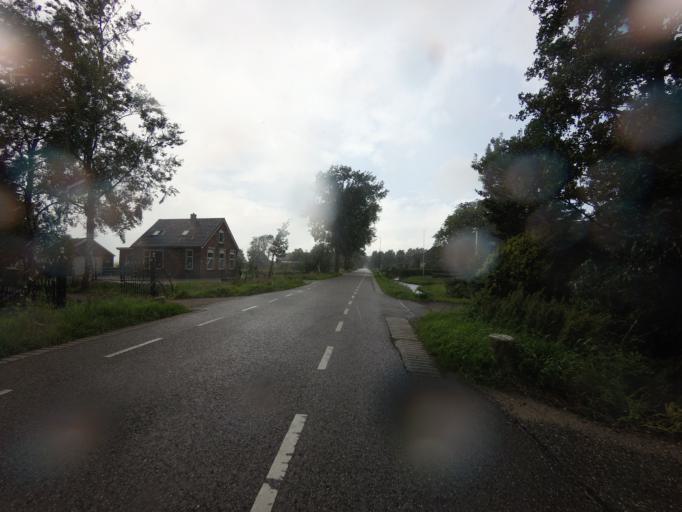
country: NL
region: North Holland
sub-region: Gemeente Wijdemeren
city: Nieuw-Loosdrecht
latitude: 52.1485
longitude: 5.1414
